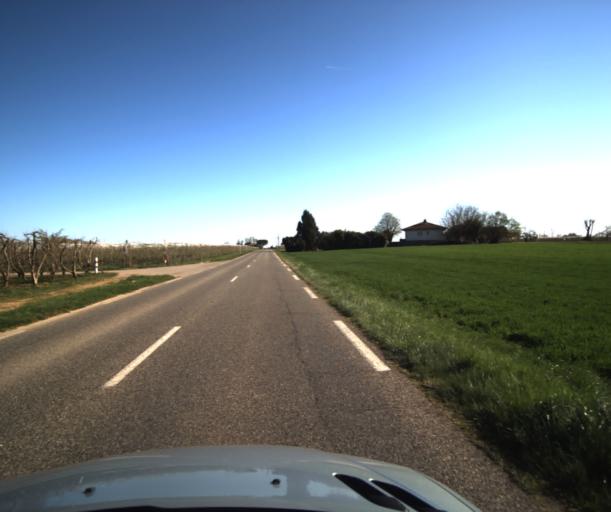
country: FR
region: Midi-Pyrenees
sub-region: Departement du Tarn-et-Garonne
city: Corbarieu
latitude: 43.9490
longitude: 1.3503
